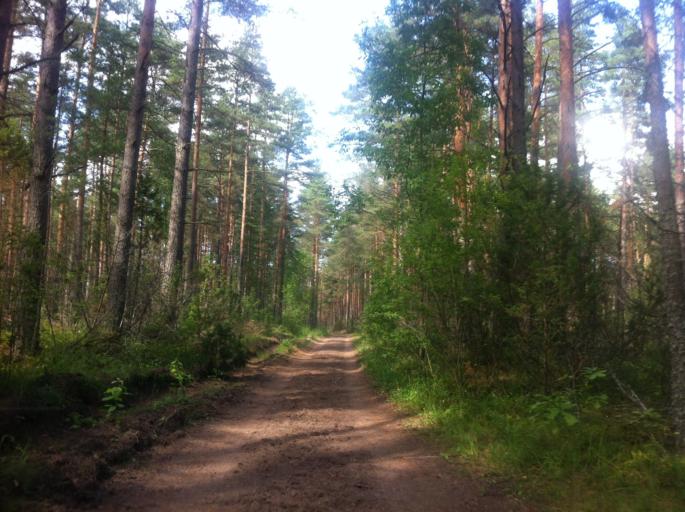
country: RU
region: Pskov
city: Izborsk
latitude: 57.8230
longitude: 27.9393
